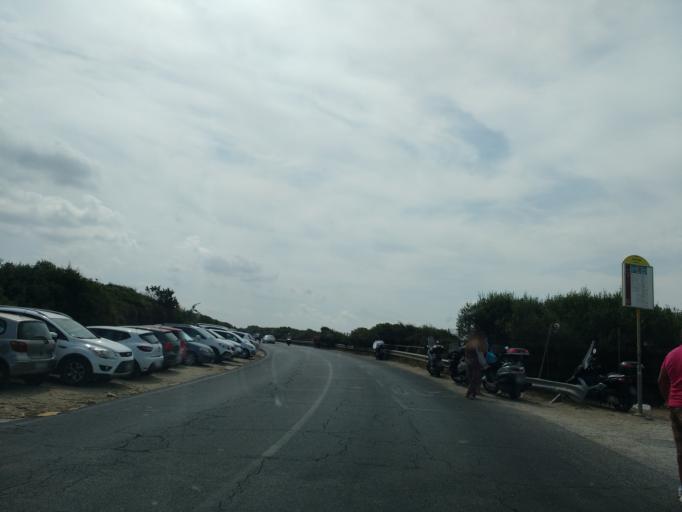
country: IT
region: Latium
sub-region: Citta metropolitana di Roma Capitale
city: Torvaianica
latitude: 41.6652
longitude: 12.4049
